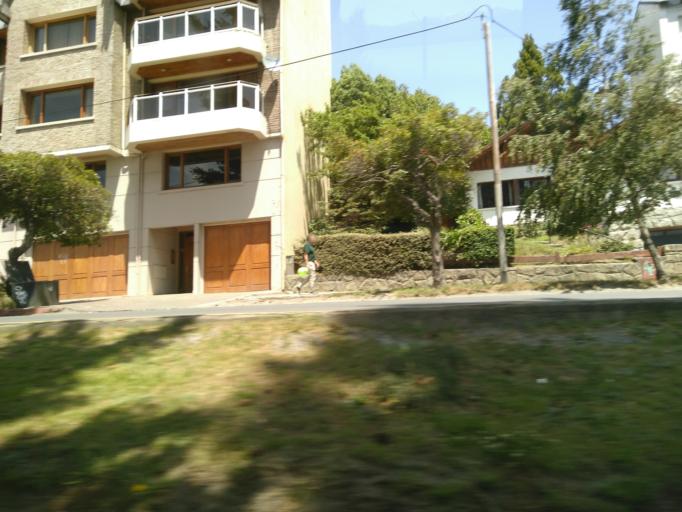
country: AR
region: Rio Negro
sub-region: Departamento de Bariloche
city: San Carlos de Bariloche
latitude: -41.1327
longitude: -71.3071
